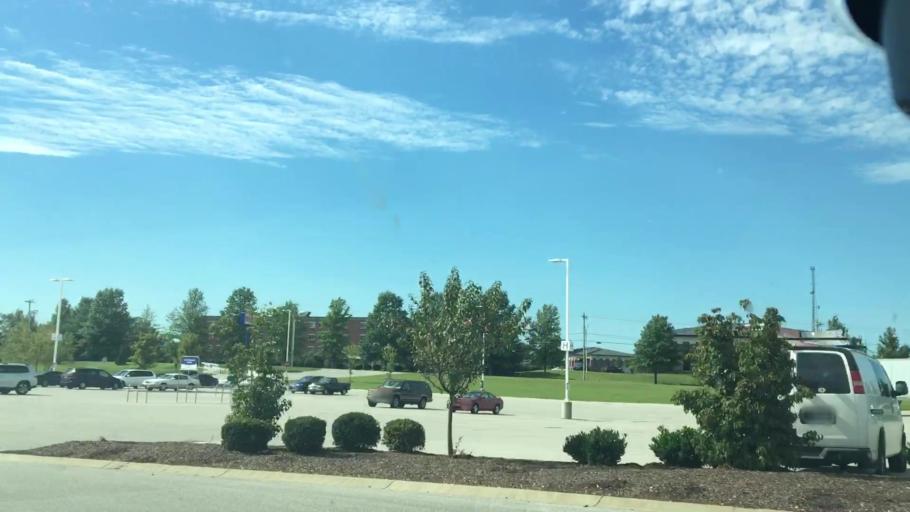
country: US
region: Kentucky
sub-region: Daviess County
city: Owensboro
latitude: 37.7568
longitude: -87.0744
